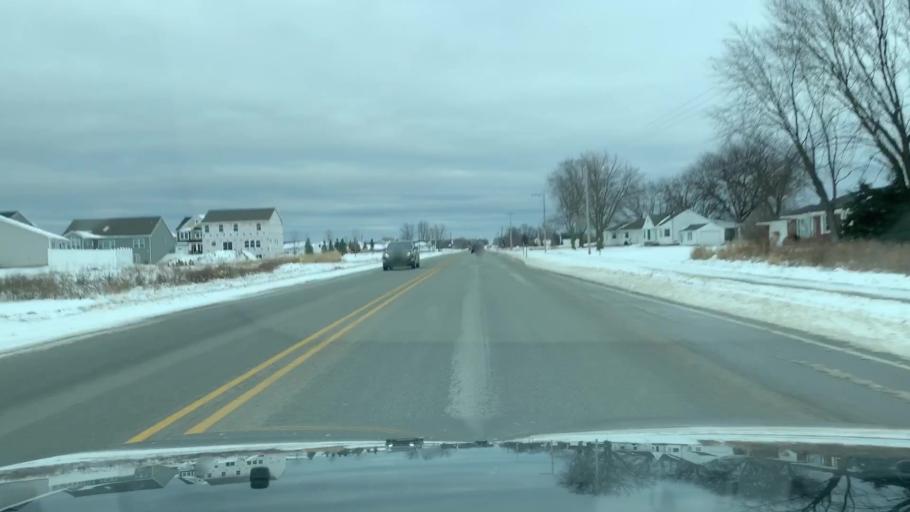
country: US
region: Michigan
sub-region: Ottawa County
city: Zeeland
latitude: 42.8122
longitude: -85.9645
